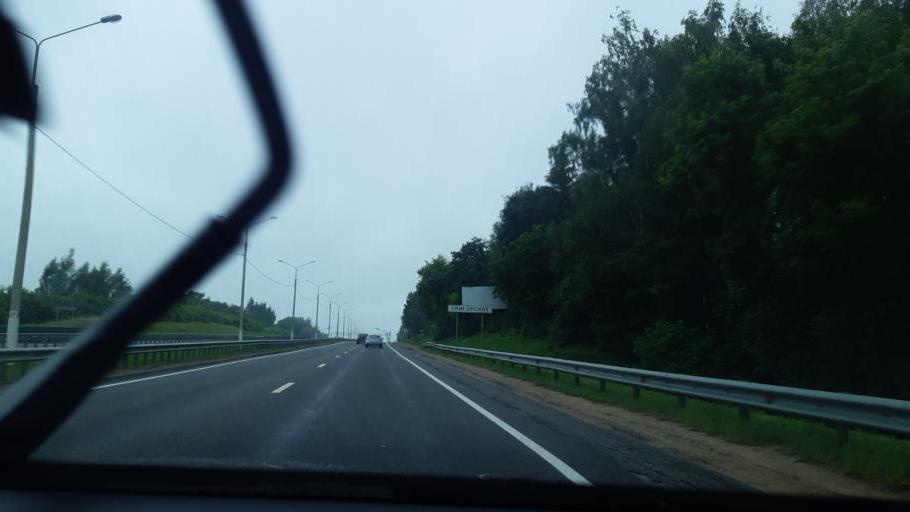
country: RU
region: Smolensk
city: Talashkino
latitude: 54.6780
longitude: 32.1432
